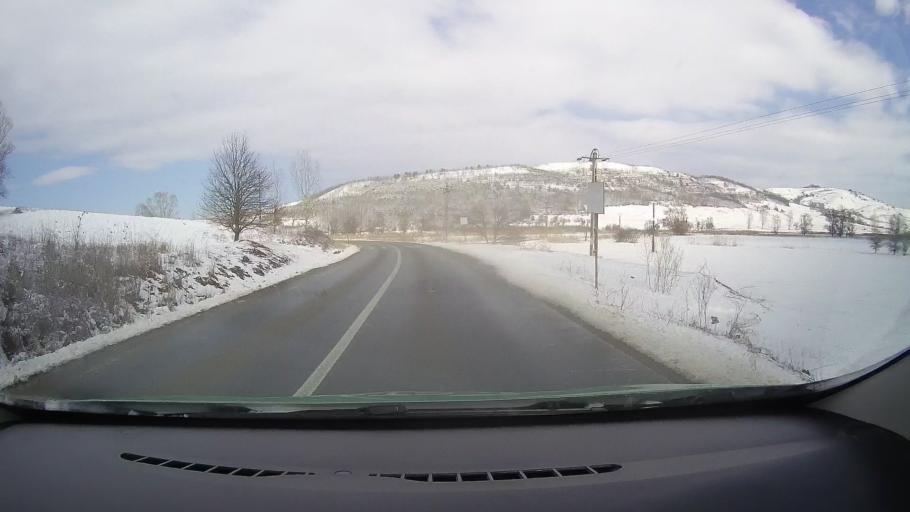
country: RO
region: Sibiu
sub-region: Comuna Altina
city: Altina
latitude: 45.9656
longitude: 24.4703
